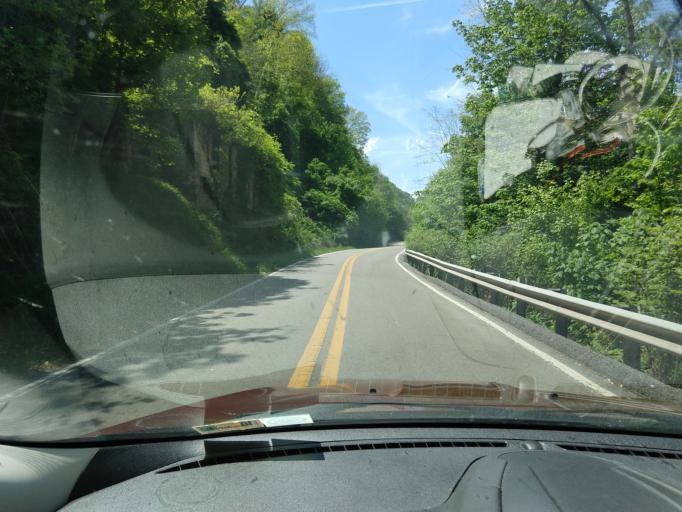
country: US
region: West Virginia
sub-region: McDowell County
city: Welch
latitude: 37.3205
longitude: -81.6926
